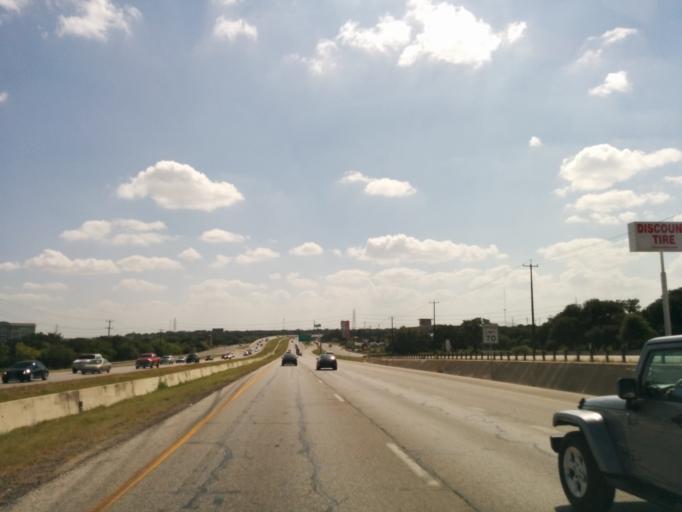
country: US
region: Texas
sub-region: Bexar County
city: Shavano Park
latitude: 29.5971
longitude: -98.5695
